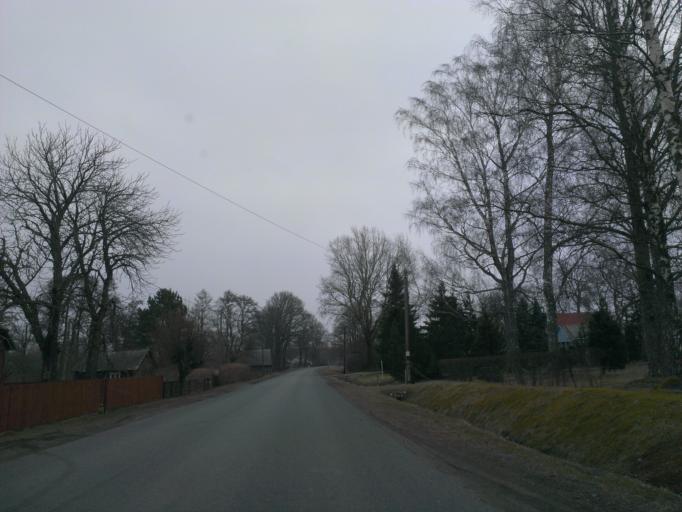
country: LV
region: Salacgrivas
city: Ainazi
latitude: 58.0033
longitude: 24.4401
